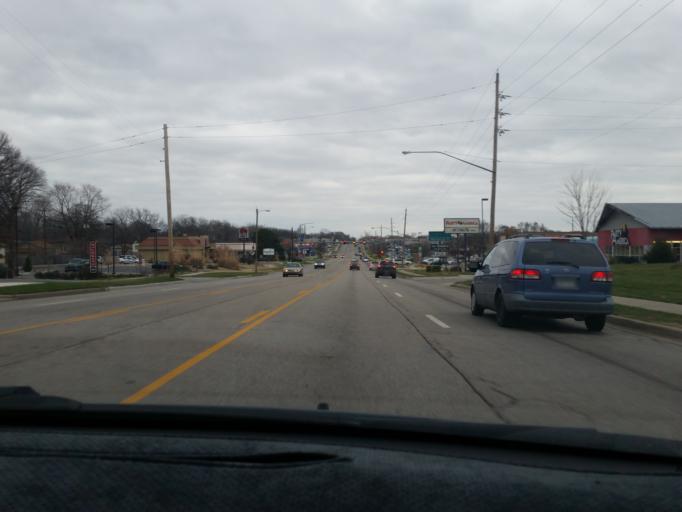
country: US
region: Kansas
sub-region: Douglas County
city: Lawrence
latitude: 38.9428
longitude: -95.2531
